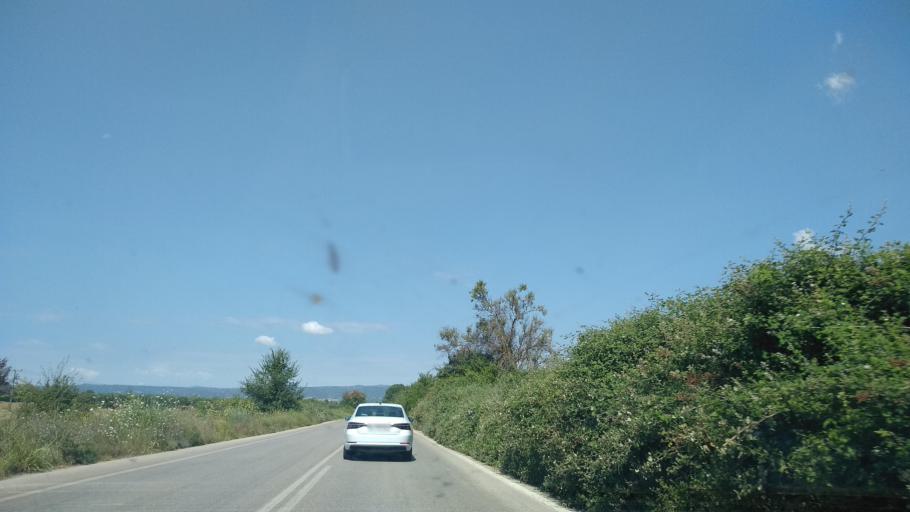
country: GR
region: Central Macedonia
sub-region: Nomos Thessalonikis
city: Nea Apollonia
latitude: 40.6291
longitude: 23.5294
